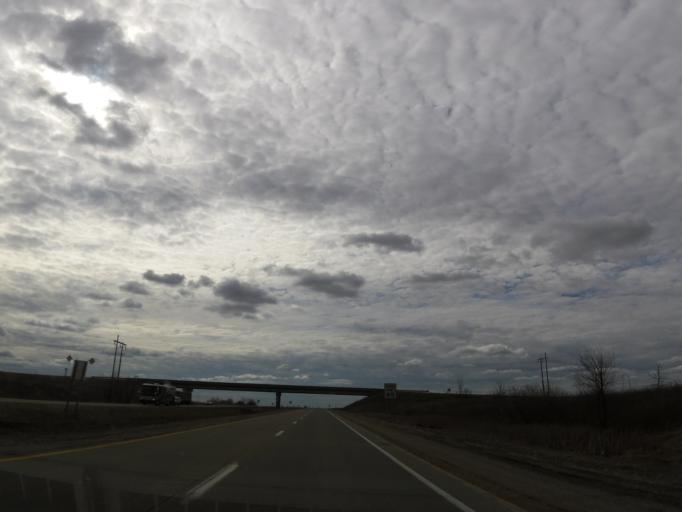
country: US
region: Iowa
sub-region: Chickasaw County
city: New Hampton
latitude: 43.0852
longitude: -92.3154
